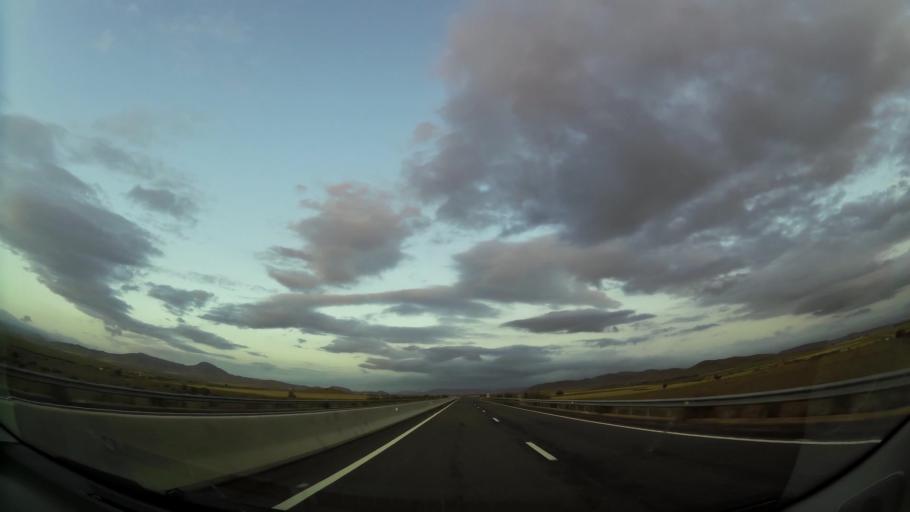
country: MA
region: Oriental
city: El Aioun
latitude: 34.6011
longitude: -2.7393
